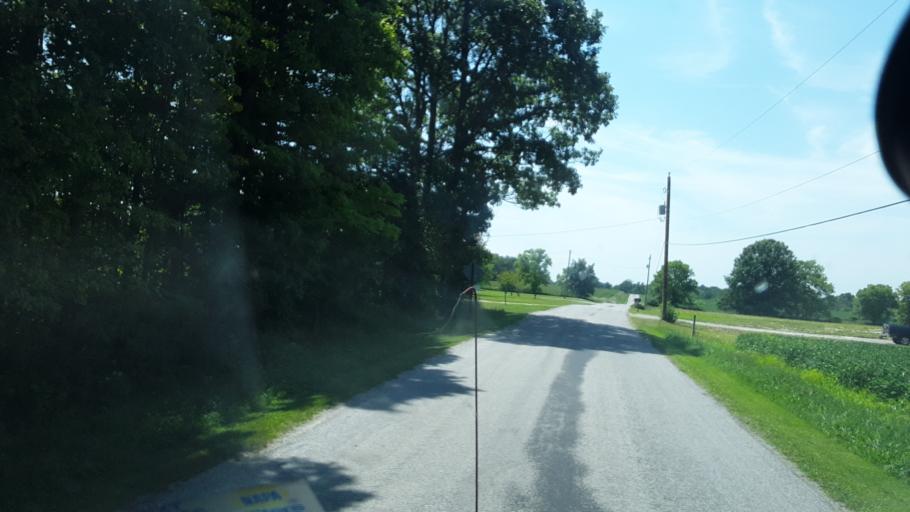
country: US
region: Ohio
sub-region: Hardin County
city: Forest
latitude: 40.7763
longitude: -83.5648
